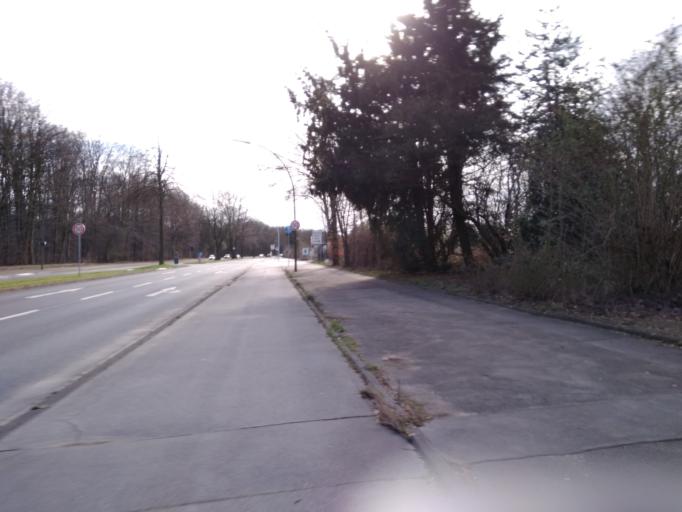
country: DE
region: North Rhine-Westphalia
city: Marl
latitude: 51.5969
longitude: 7.0659
